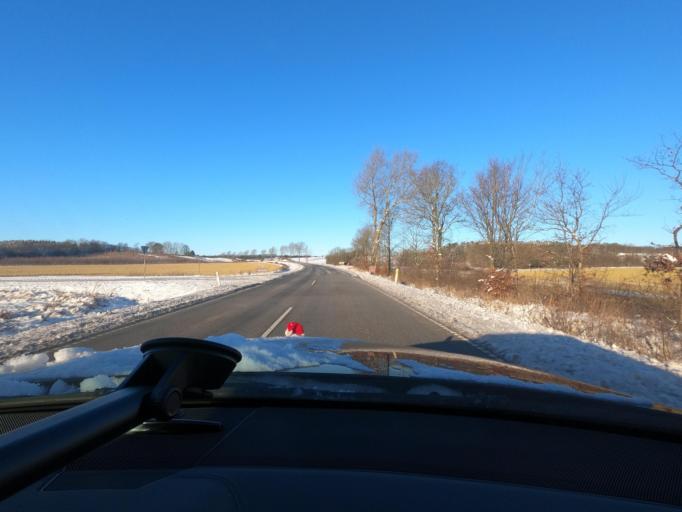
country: DK
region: South Denmark
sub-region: Aabenraa Kommune
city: Rodekro
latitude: 55.0813
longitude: 9.2196
